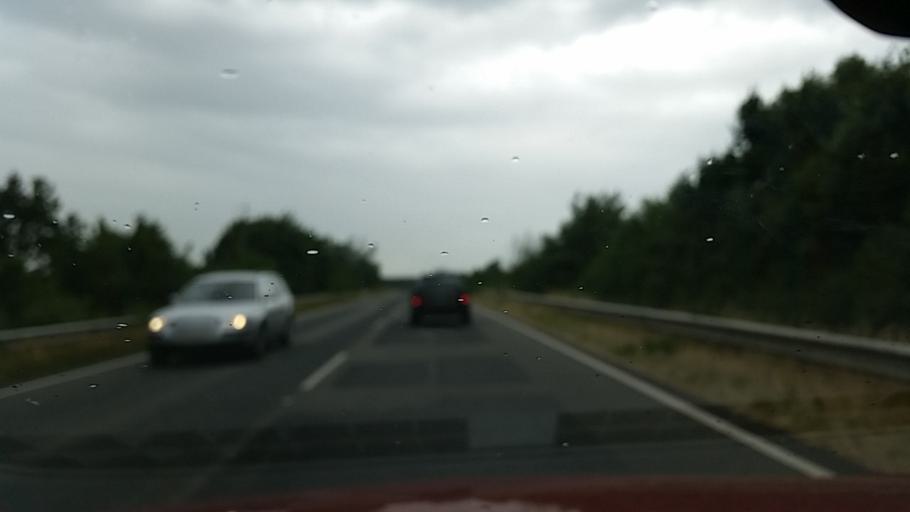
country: DE
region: Lower Saxony
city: Wagenhoff
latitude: 52.5141
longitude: 10.5201
